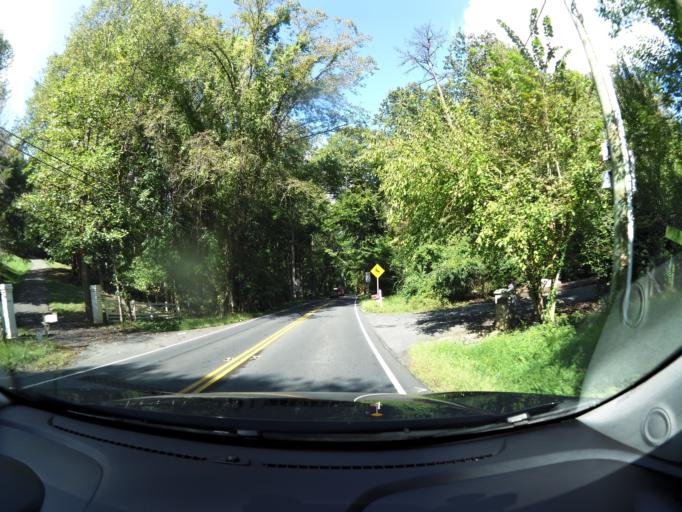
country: US
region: Virginia
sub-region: Fairfax County
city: Great Falls
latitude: 38.9736
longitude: -77.2437
